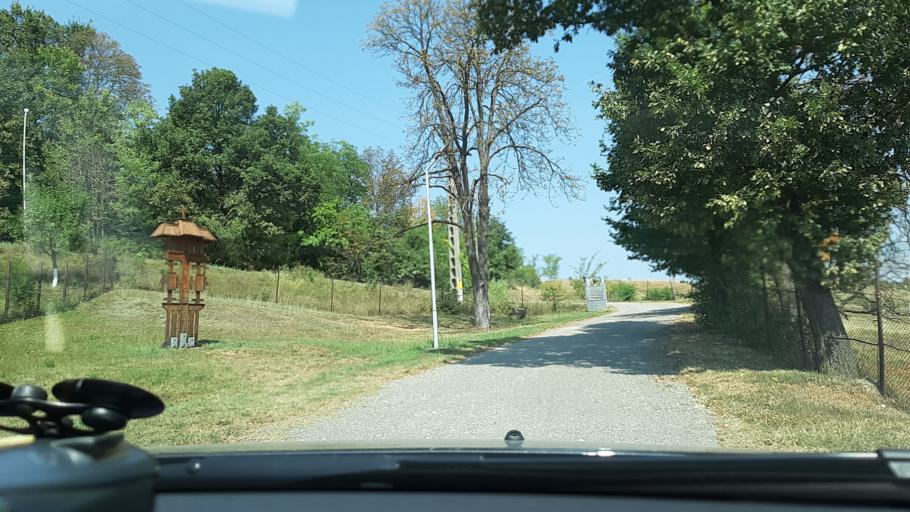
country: RO
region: Gorj
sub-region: Comuna Targu Carbunesti
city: Targu Carbunesti
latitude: 44.9630
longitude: 23.5208
